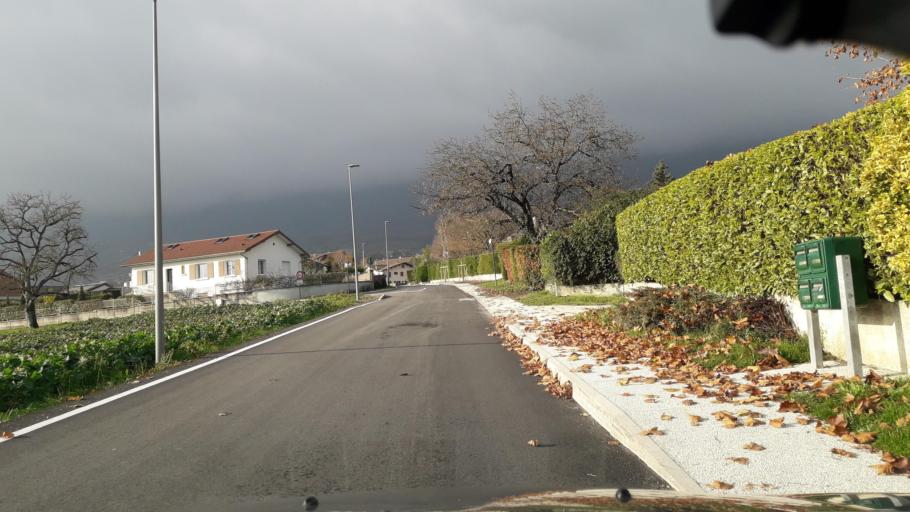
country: FR
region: Rhone-Alpes
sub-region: Departement de l'Isere
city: Saint-Nazaire-les-Eymes
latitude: 45.2447
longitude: 5.8420
